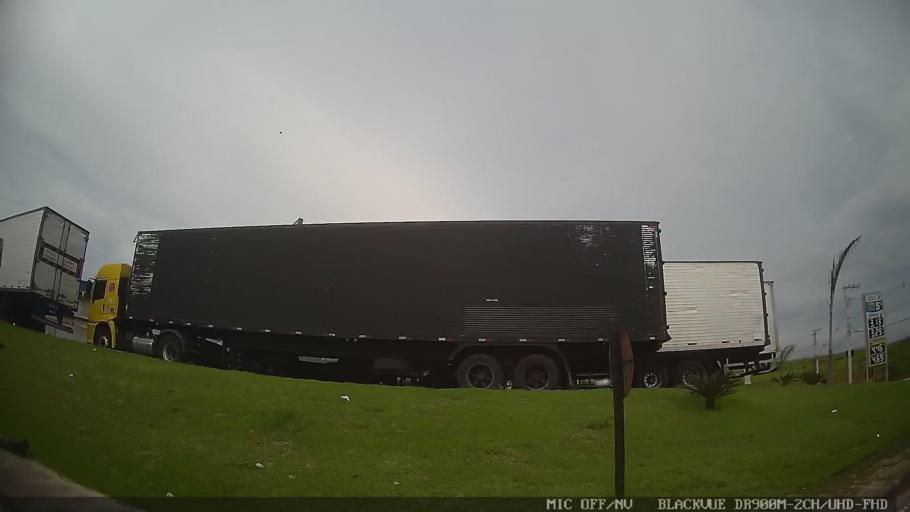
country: BR
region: Sao Paulo
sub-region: Aruja
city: Aruja
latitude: -23.4329
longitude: -46.2667
